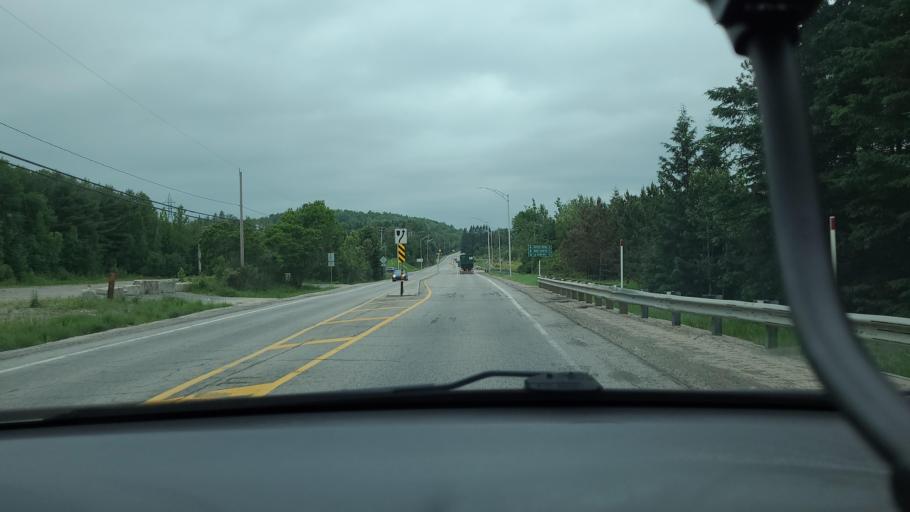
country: CA
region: Quebec
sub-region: Laurentides
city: Labelle
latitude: 46.2960
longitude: -74.7766
